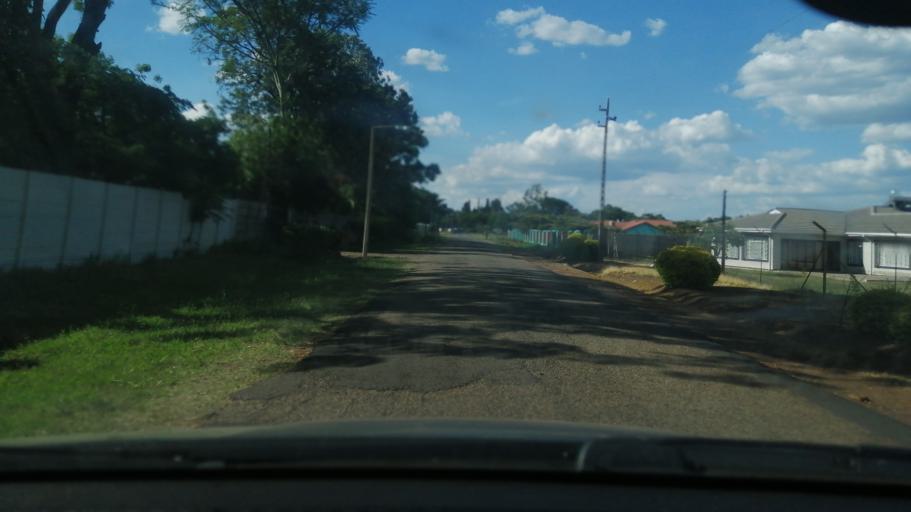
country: ZW
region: Harare
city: Harare
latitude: -17.7708
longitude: 31.0628
